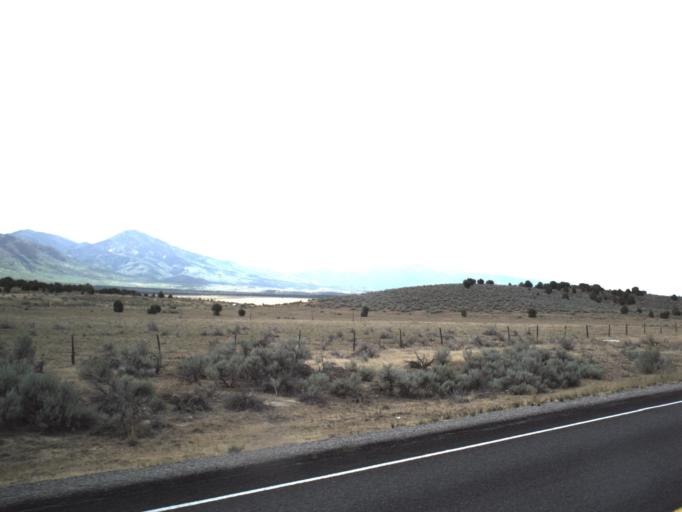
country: US
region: Utah
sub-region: Millard County
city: Fillmore
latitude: 39.1426
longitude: -112.2392
